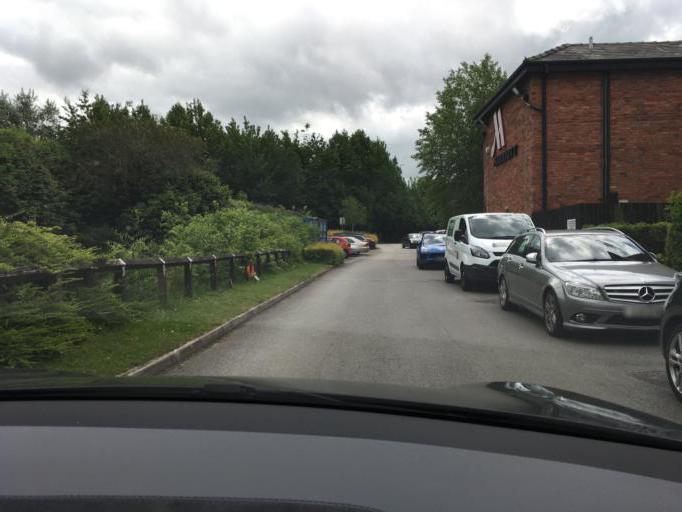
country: GB
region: England
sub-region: Manchester
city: Ringway
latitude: 53.3650
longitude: -2.2965
